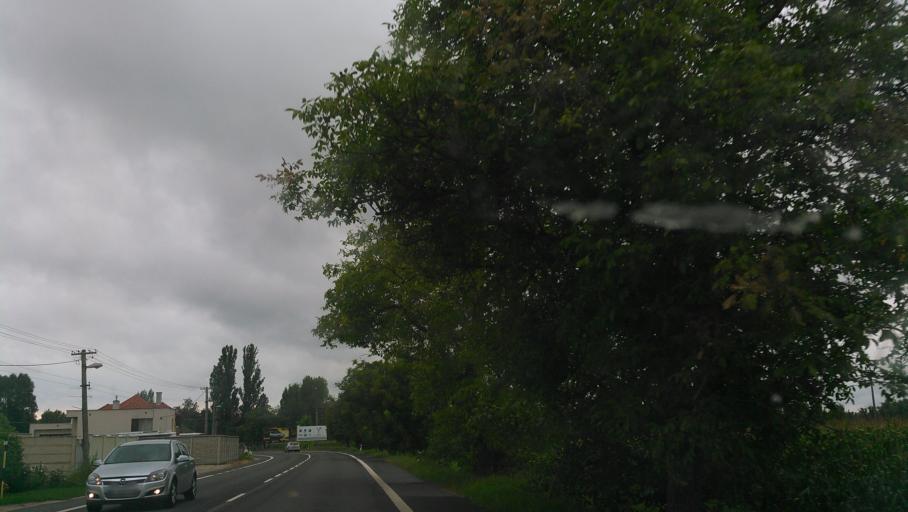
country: SK
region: Trnavsky
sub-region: Okres Dunajska Streda
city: Velky Meder
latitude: 47.9460
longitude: 17.7142
